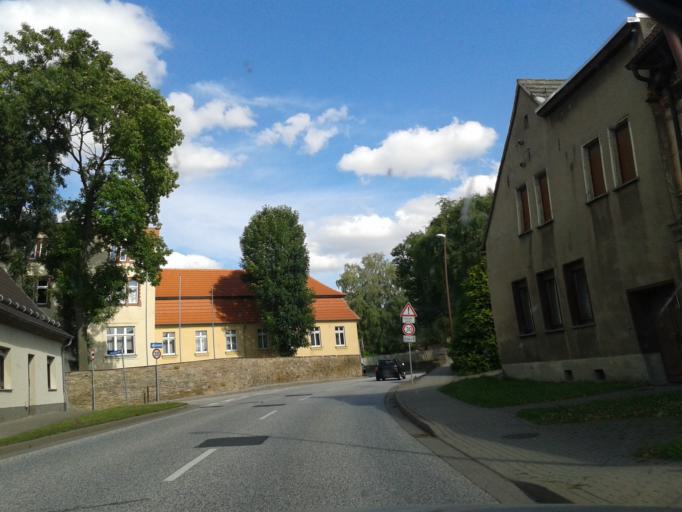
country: DE
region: Saxony-Anhalt
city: Klostermansfeld
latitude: 51.5833
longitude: 11.4963
